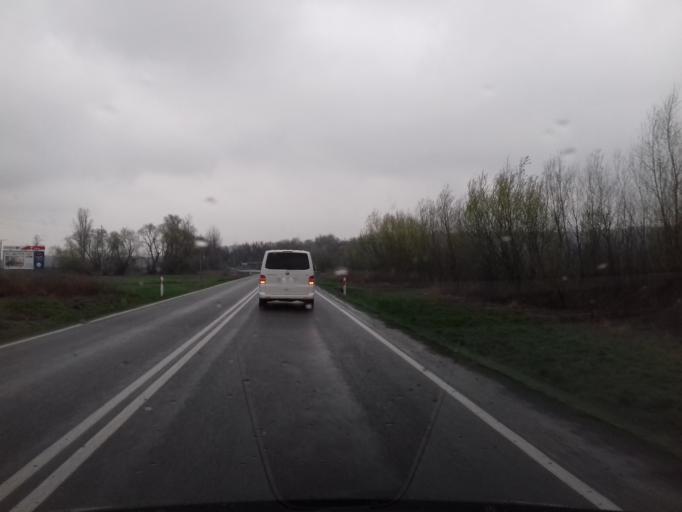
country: PL
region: Lesser Poland Voivodeship
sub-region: Powiat nowosadecki
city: Stary Sacz
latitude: 49.5492
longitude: 20.6530
